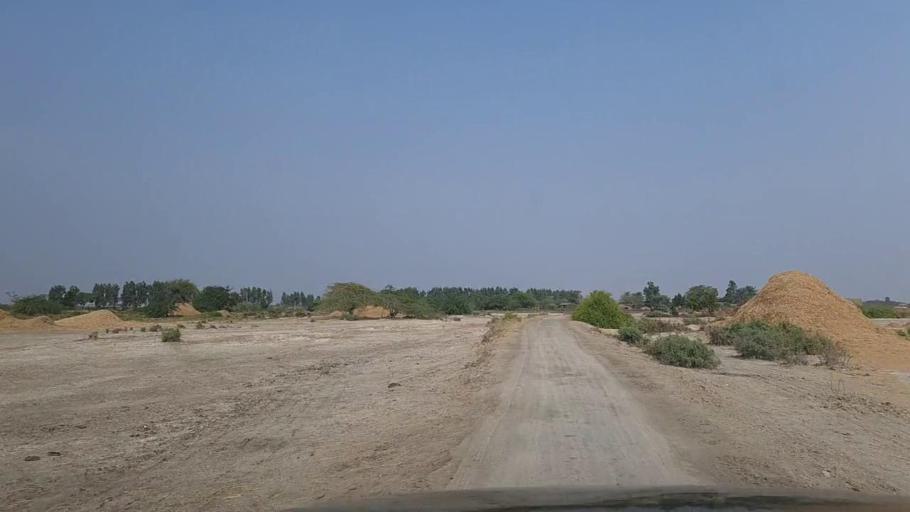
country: PK
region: Sindh
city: Thatta
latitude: 24.7516
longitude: 67.7982
